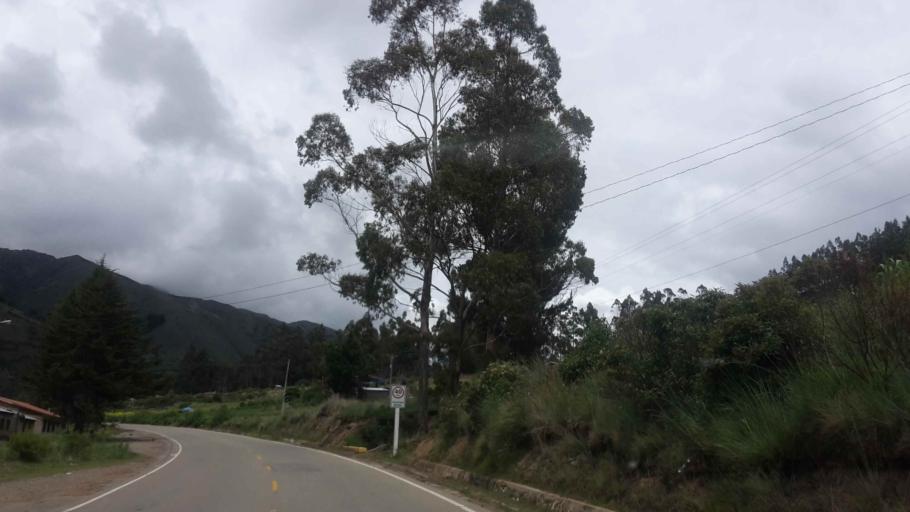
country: BO
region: Cochabamba
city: Arani
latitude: -17.4914
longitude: -65.4526
